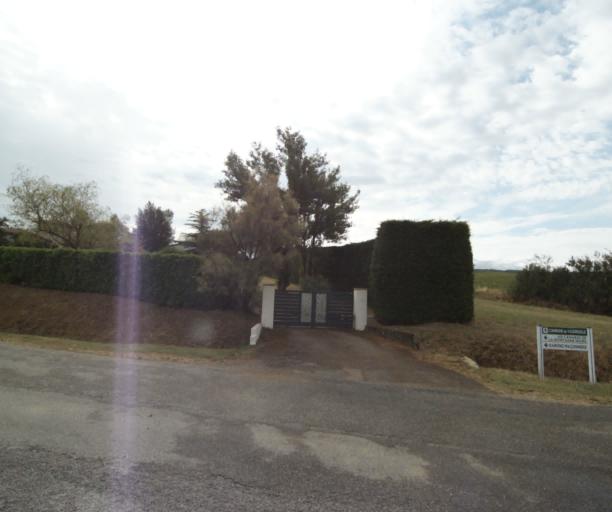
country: FR
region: Midi-Pyrenees
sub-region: Departement de la Haute-Garonne
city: Revel
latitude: 43.4241
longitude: 1.9826
